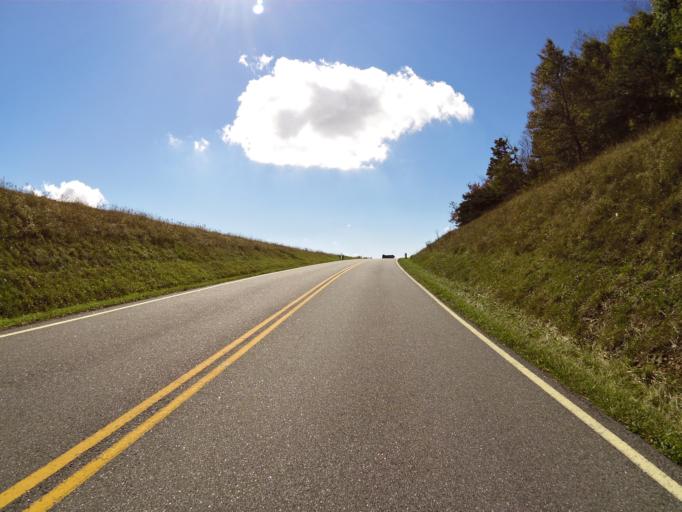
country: US
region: Virginia
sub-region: Page County
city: Stanley
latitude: 38.5187
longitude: -78.4332
